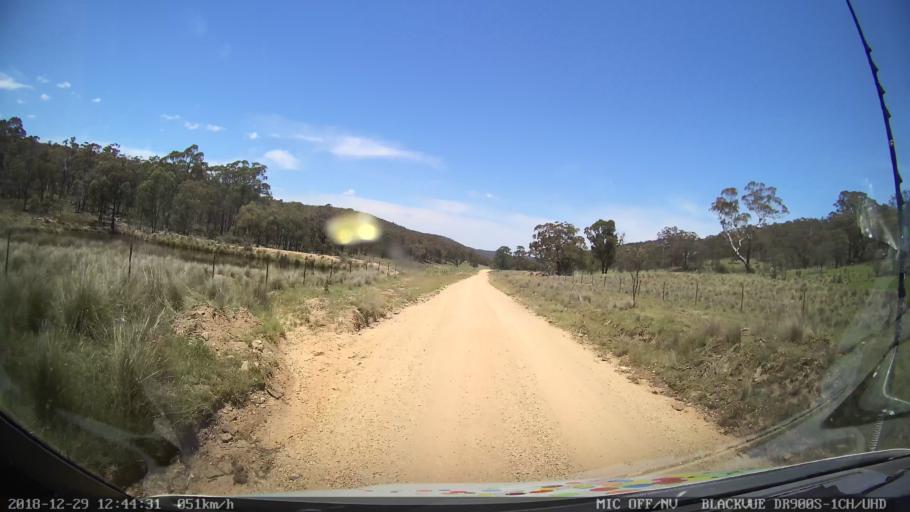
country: AU
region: Australian Capital Territory
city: Macarthur
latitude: -35.6278
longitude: 149.2160
